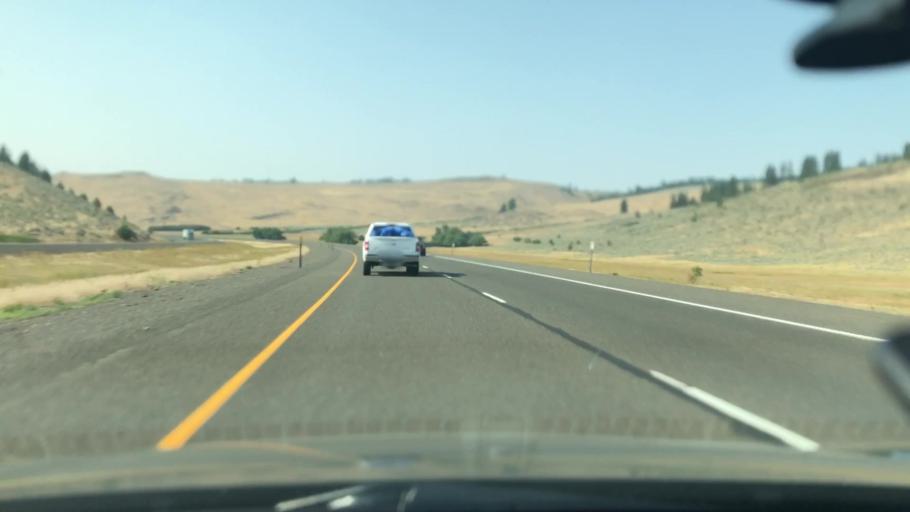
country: US
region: Oregon
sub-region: Union County
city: Union
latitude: 45.1647
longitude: -117.9643
